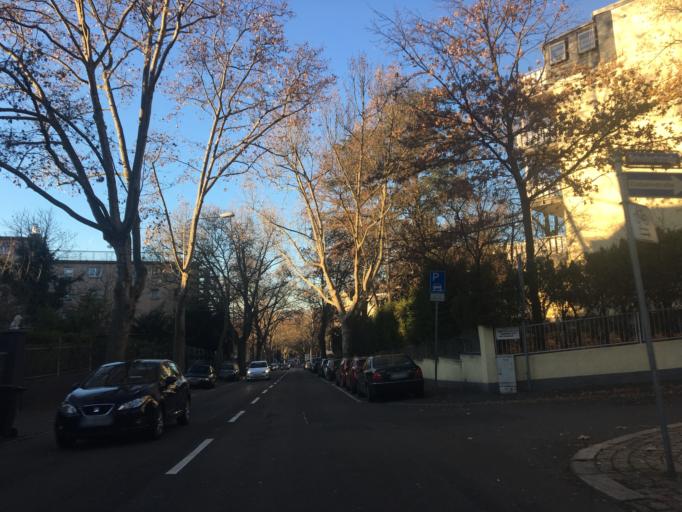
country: DE
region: Hesse
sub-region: Regierungsbezirk Darmstadt
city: Wiesbaden
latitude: 50.0763
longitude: 8.2517
